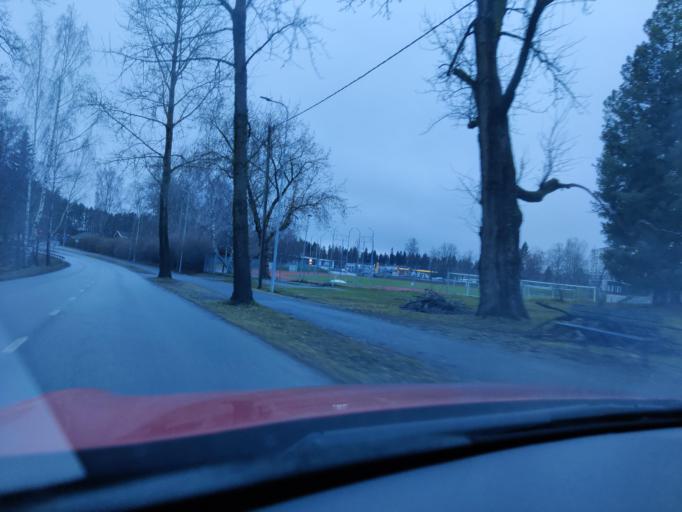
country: FI
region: Pirkanmaa
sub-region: Tampere
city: Nokia
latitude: 61.4820
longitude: 23.5295
